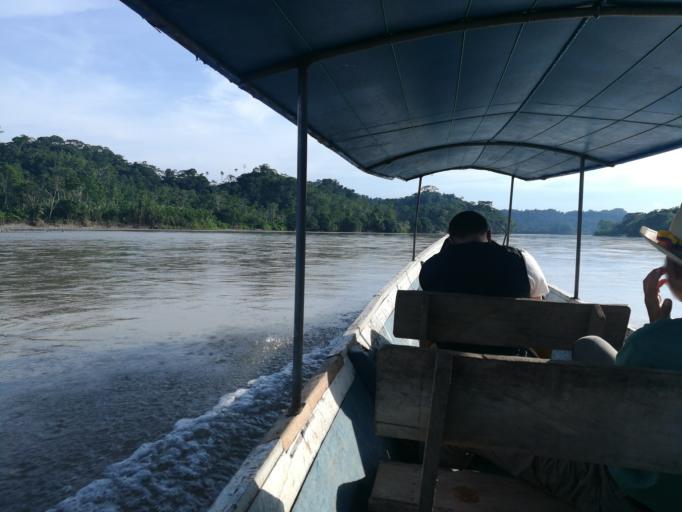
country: EC
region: Orellana
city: Boca Suno
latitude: -0.8552
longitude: -77.2441
